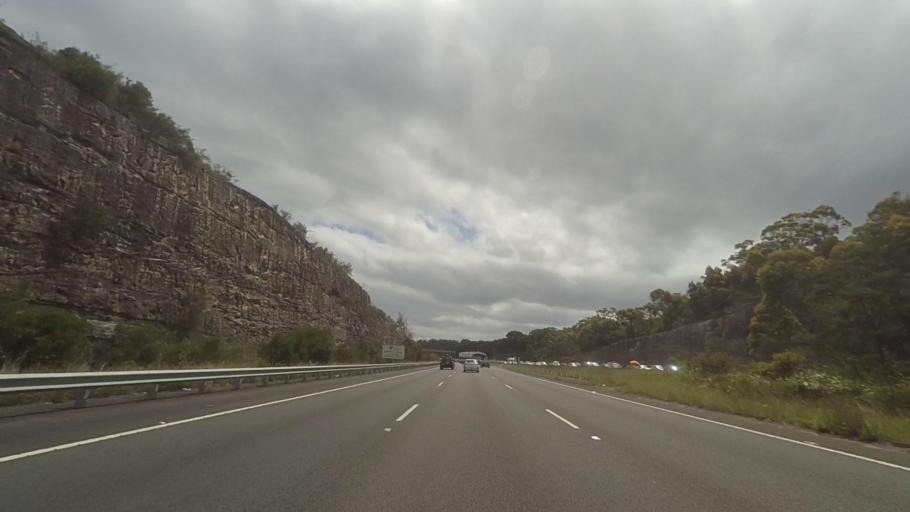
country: AU
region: New South Wales
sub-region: Gosford Shire
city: Point Clare
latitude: -33.4525
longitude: 151.2110
